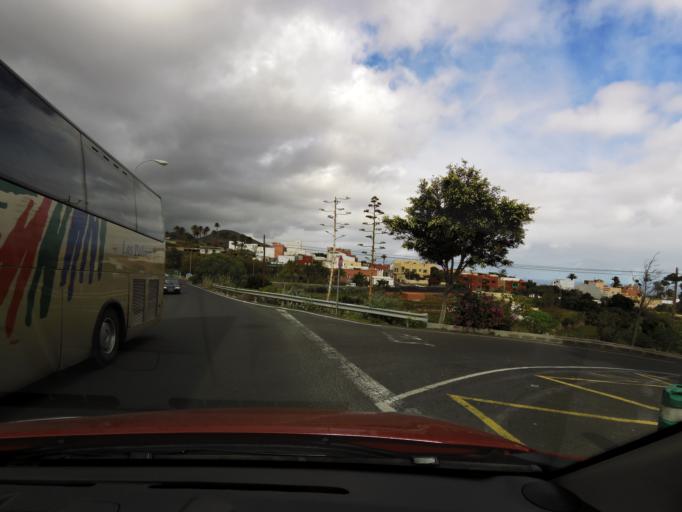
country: ES
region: Canary Islands
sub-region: Provincia de Las Palmas
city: Ingenio
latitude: 27.9246
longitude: -15.4344
